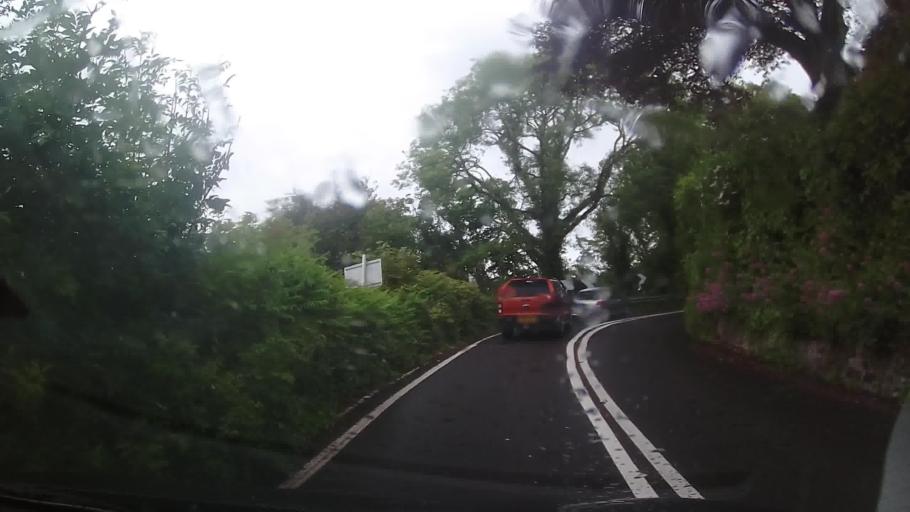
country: GB
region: England
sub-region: Devon
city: Dartmouth
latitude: 50.3638
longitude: -3.5748
